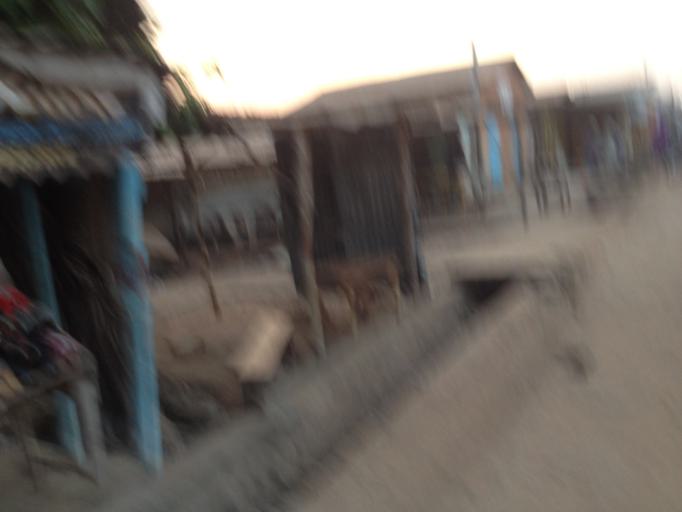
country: BJ
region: Borgou
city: Parakou
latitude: 9.3415
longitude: 2.6250
